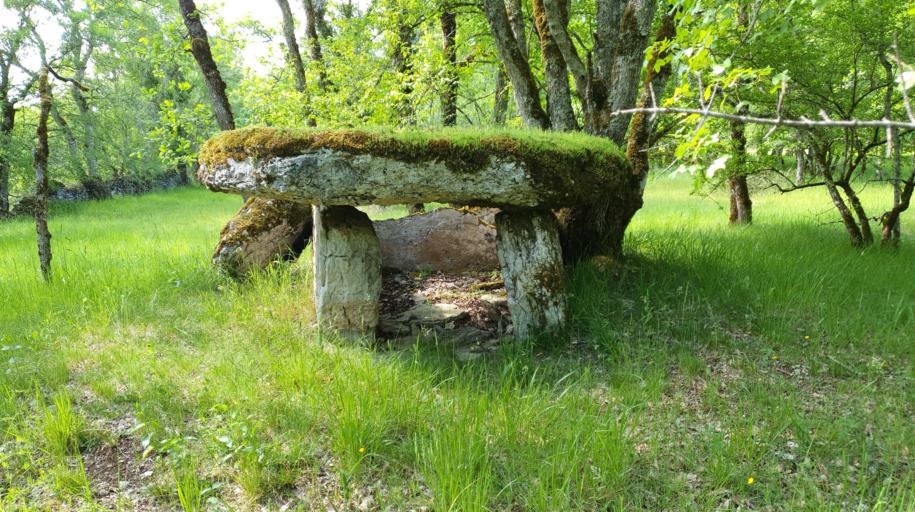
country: FR
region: Midi-Pyrenees
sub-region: Departement du Lot
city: Gramat
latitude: 44.7139
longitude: 1.7530
